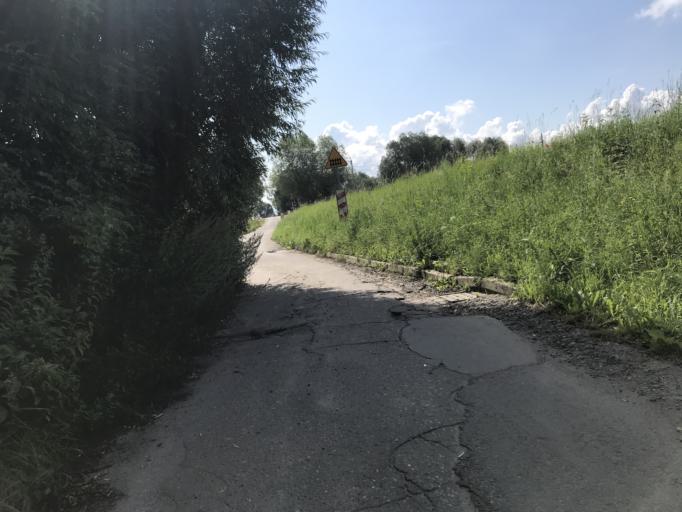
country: PL
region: Pomeranian Voivodeship
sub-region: Gdansk
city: Gdansk
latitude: 54.3261
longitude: 18.6577
